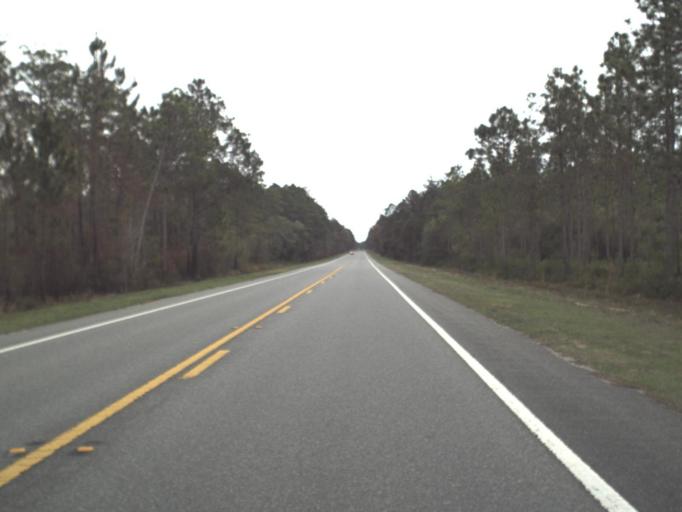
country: US
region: Florida
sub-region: Gadsden County
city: Midway
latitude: 30.3729
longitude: -84.5523
